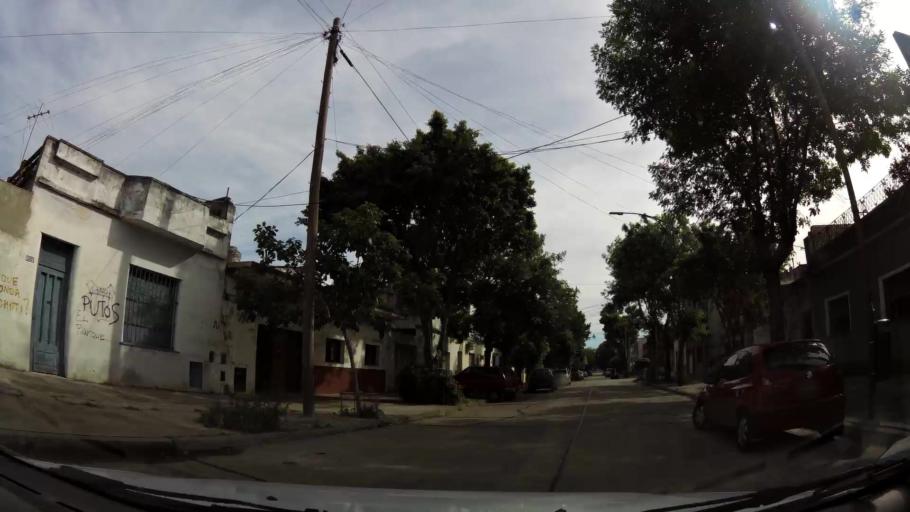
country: AR
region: Buenos Aires F.D.
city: Villa Lugano
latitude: -34.6521
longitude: -58.4794
